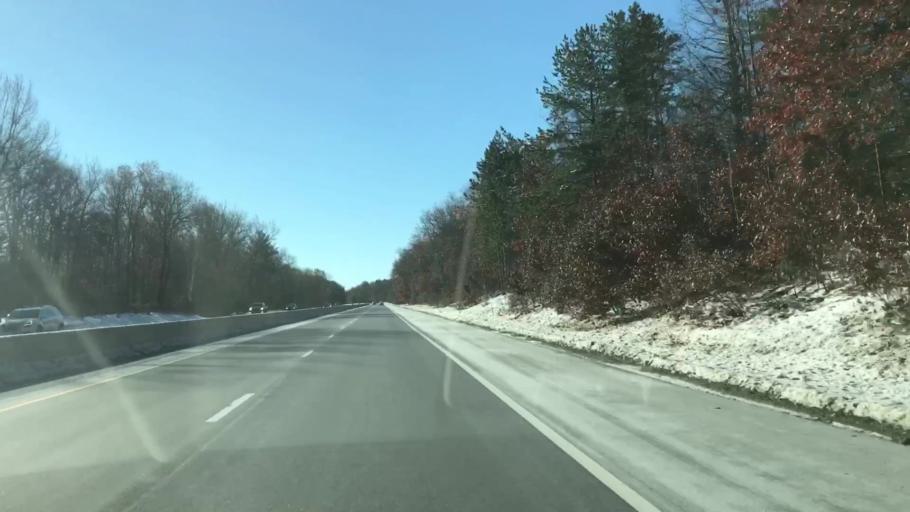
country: US
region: New Hampshire
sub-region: Hillsborough County
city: Pinardville
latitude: 43.0315
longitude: -71.4872
